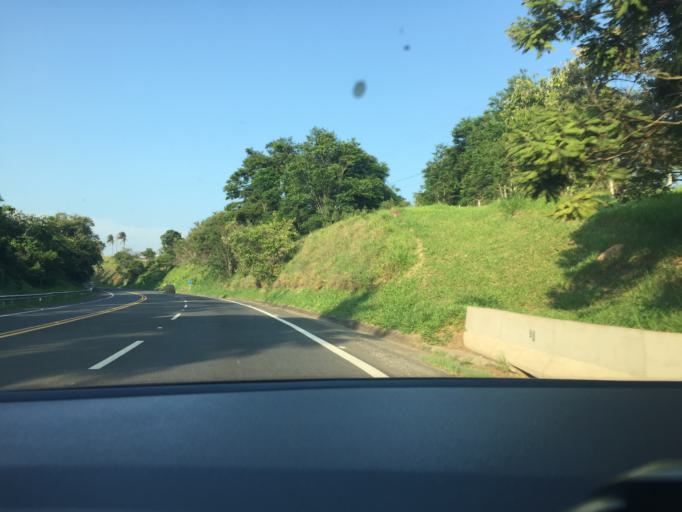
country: BR
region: Sao Paulo
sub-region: Louveira
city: Louveira
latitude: -23.0793
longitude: -46.9088
